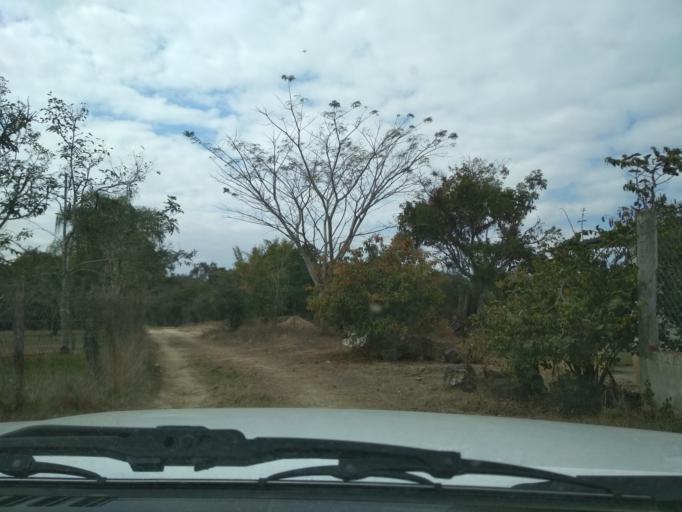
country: MX
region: Veracruz
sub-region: Coatepec
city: Tuzamapan
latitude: 19.3701
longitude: -96.8768
